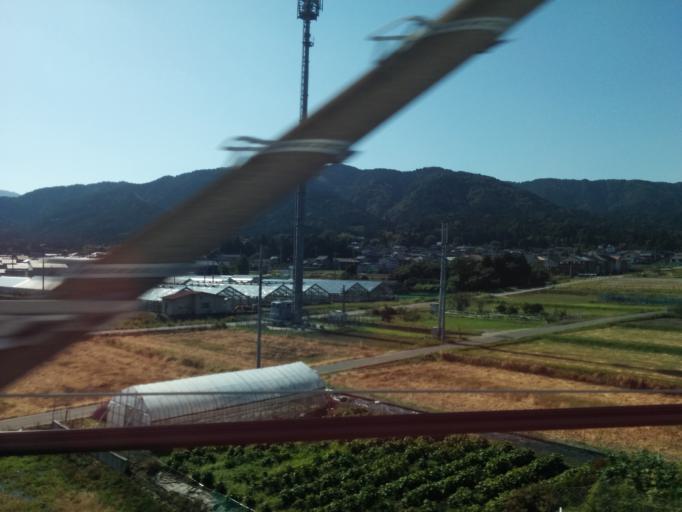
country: JP
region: Gifu
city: Tarui
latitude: 35.3628
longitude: 136.5335
